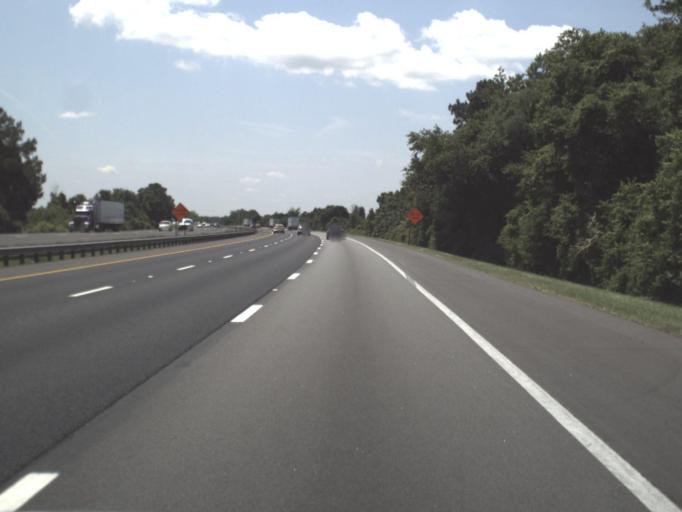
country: US
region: Florida
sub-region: Nassau County
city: Yulee
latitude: 30.5836
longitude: -81.6472
